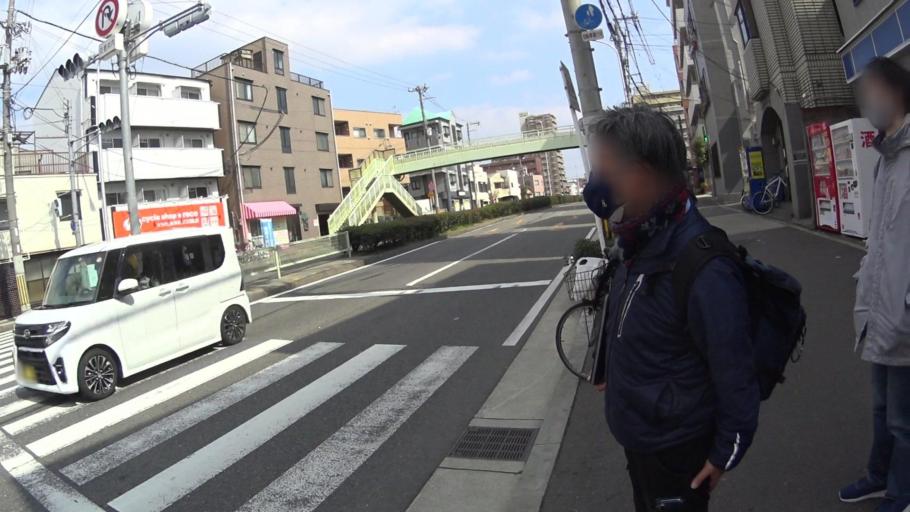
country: JP
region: Osaka
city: Sakai
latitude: 34.6092
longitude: 135.4952
